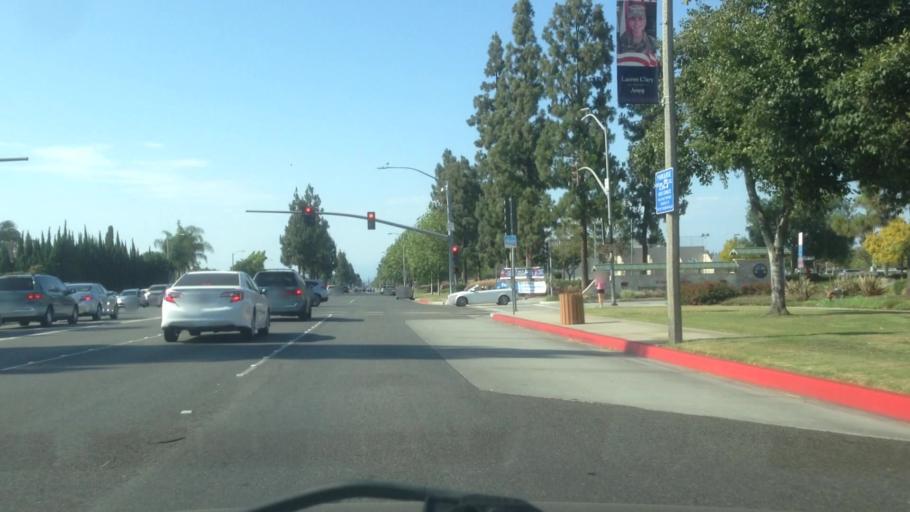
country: US
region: California
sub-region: Orange County
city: Fountain Valley
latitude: 33.7231
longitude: -117.9545
